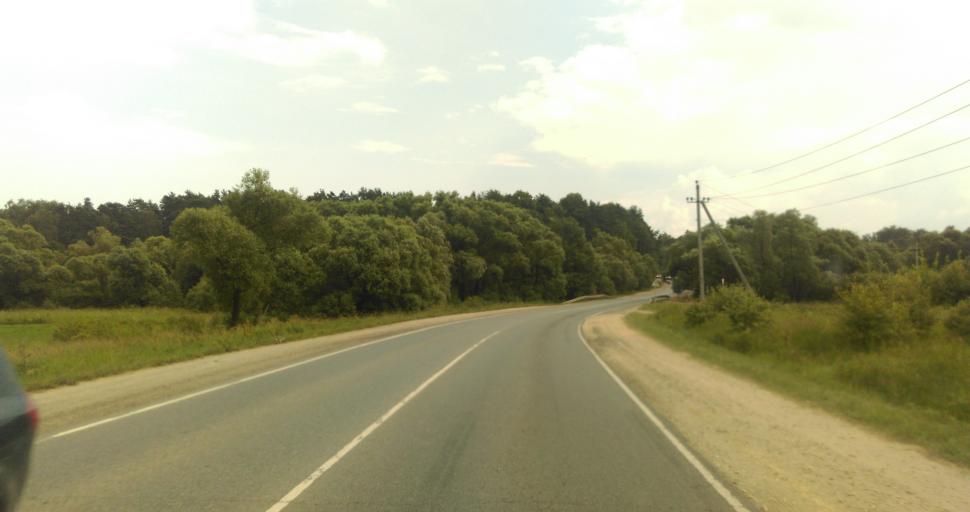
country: RU
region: Moskovskaya
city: Zhitnevo
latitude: 55.3697
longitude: 37.8949
